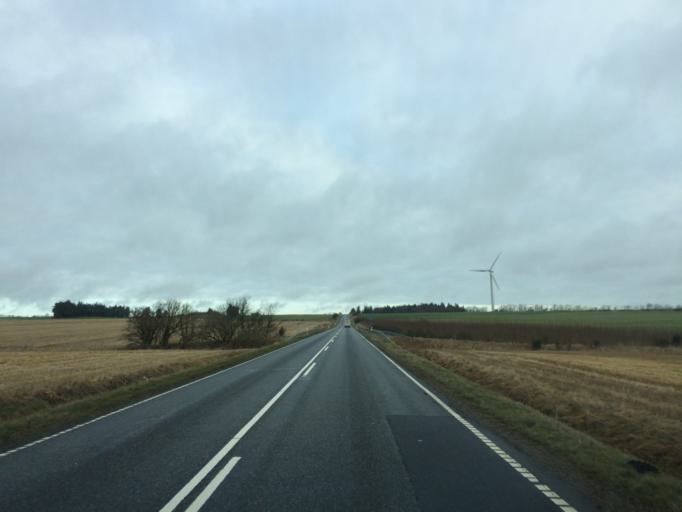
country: DK
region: Central Jutland
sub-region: Struer Kommune
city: Struer
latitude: 56.4209
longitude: 8.5007
